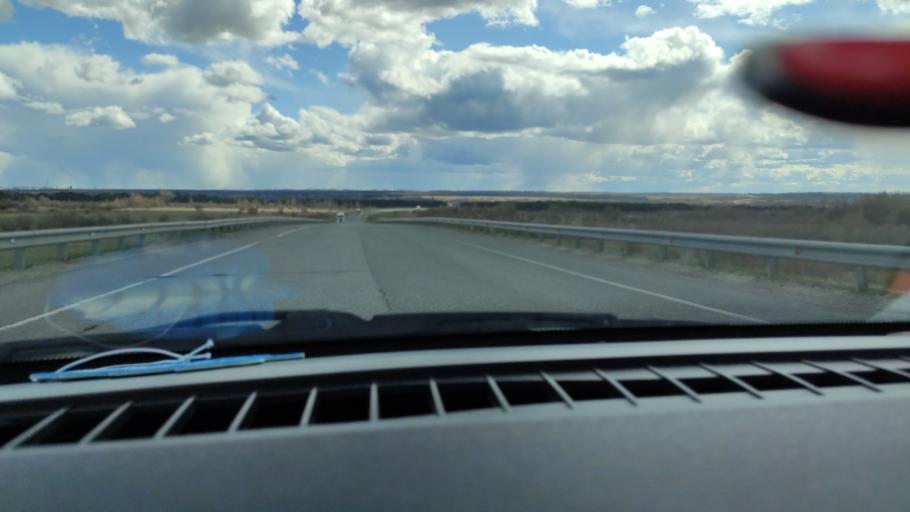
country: RU
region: Samara
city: Varlamovo
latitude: 53.1588
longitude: 48.2842
